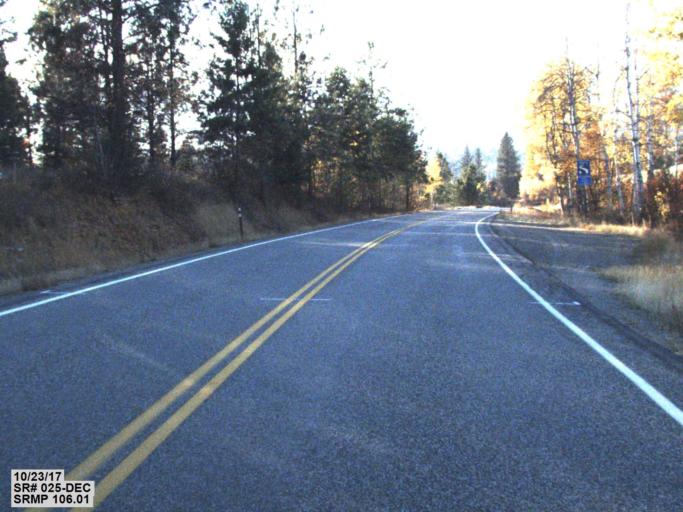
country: CA
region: British Columbia
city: Rossland
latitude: 48.8510
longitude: -117.8898
